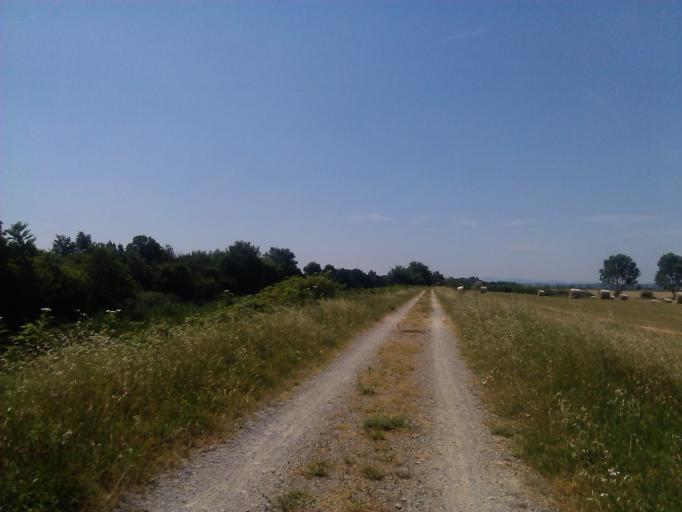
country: IT
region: Tuscany
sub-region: Province of Arezzo
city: Cesa
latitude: 43.3616
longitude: 11.8264
